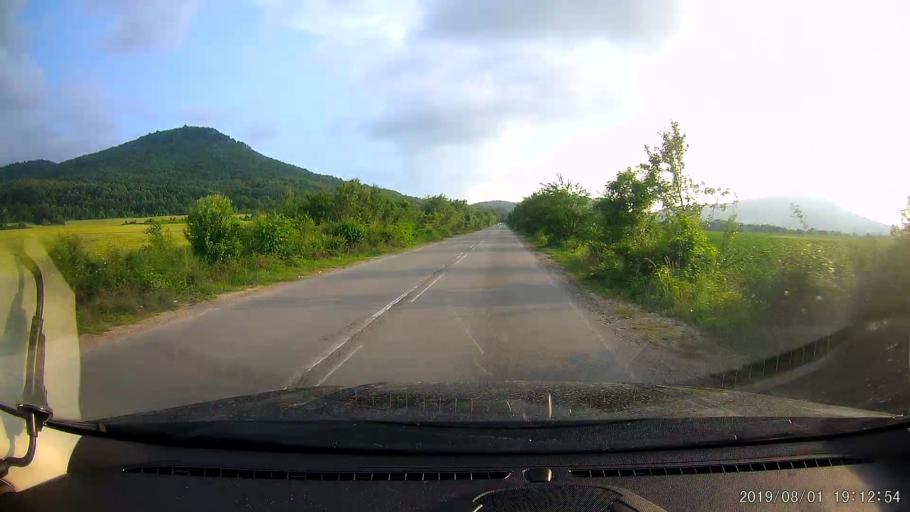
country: BG
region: Shumen
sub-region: Obshtina Smyadovo
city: Smyadovo
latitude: 42.9581
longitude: 26.9467
